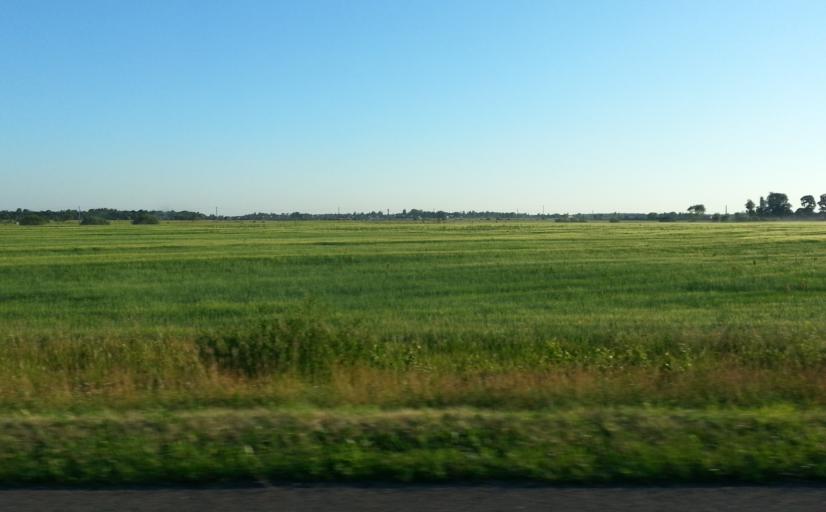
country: LT
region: Panevezys
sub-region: Panevezys City
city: Panevezys
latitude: 55.6047
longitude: 24.4364
